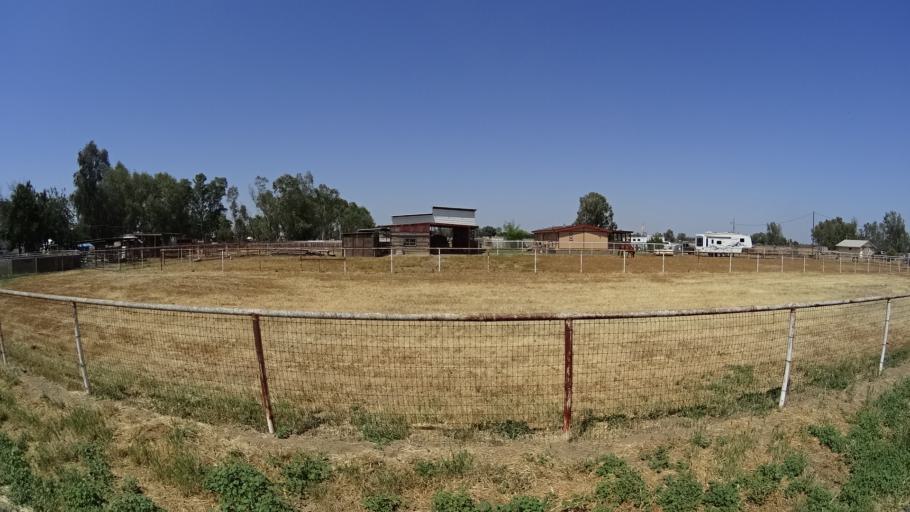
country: US
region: California
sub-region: Kings County
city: Home Garden
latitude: 36.2998
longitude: -119.6100
